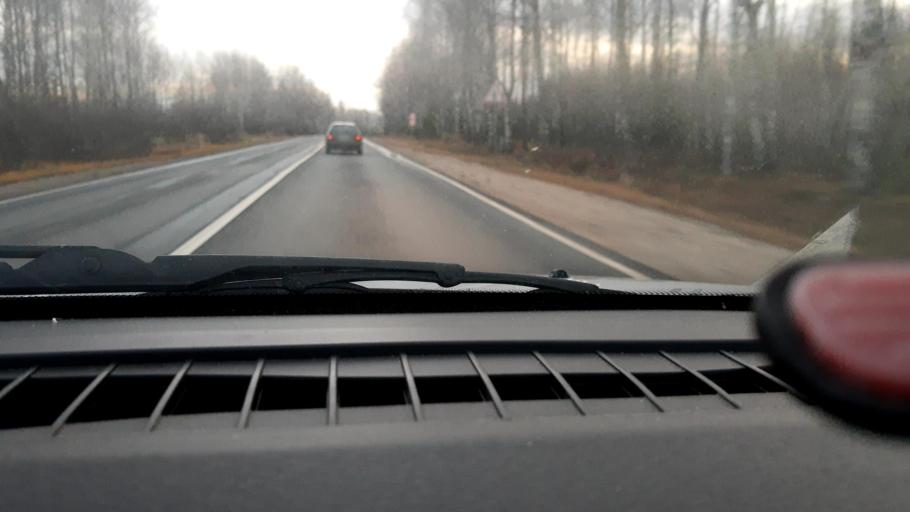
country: RU
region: Nizjnij Novgorod
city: Krasnyye Baki
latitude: 57.0786
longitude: 45.1444
